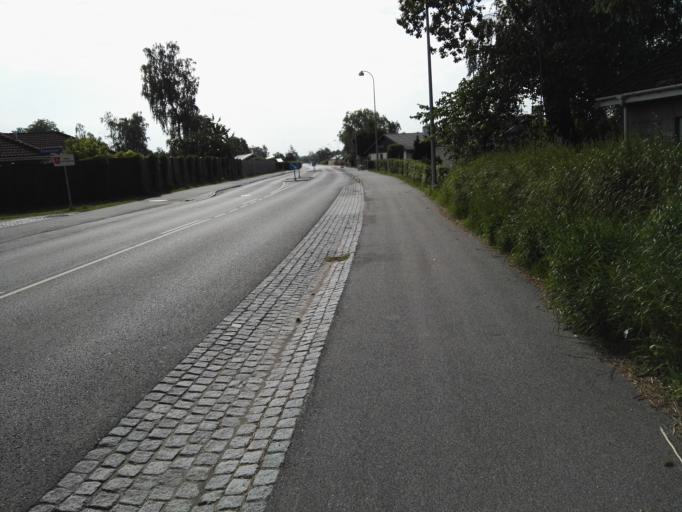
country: DK
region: Zealand
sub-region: Roskilde Kommune
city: Jyllinge
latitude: 55.7719
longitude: 12.1003
